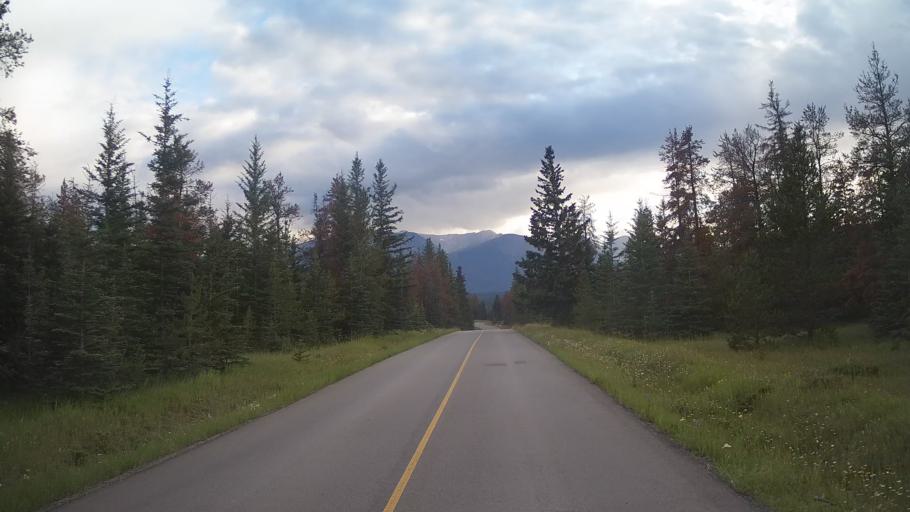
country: CA
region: Alberta
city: Jasper Park Lodge
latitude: 52.9269
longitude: -118.0320
